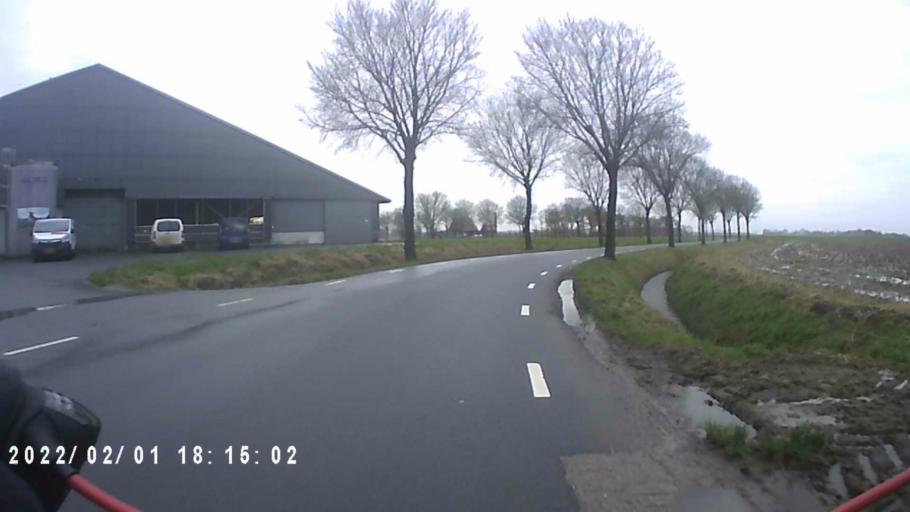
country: NL
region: Groningen
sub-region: Gemeente De Marne
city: Ulrum
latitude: 53.3480
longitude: 6.3349
